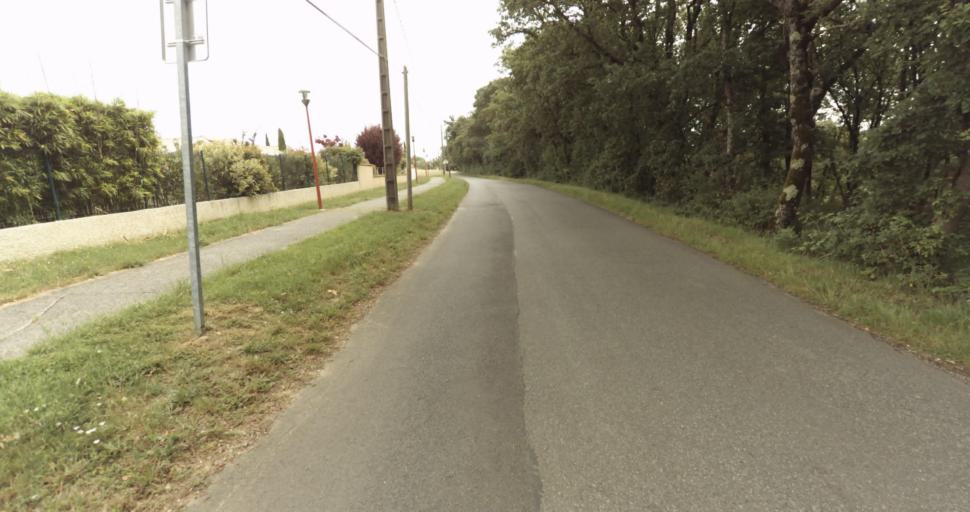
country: FR
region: Midi-Pyrenees
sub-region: Departement de la Haute-Garonne
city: Fontenilles
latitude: 43.5536
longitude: 1.2011
